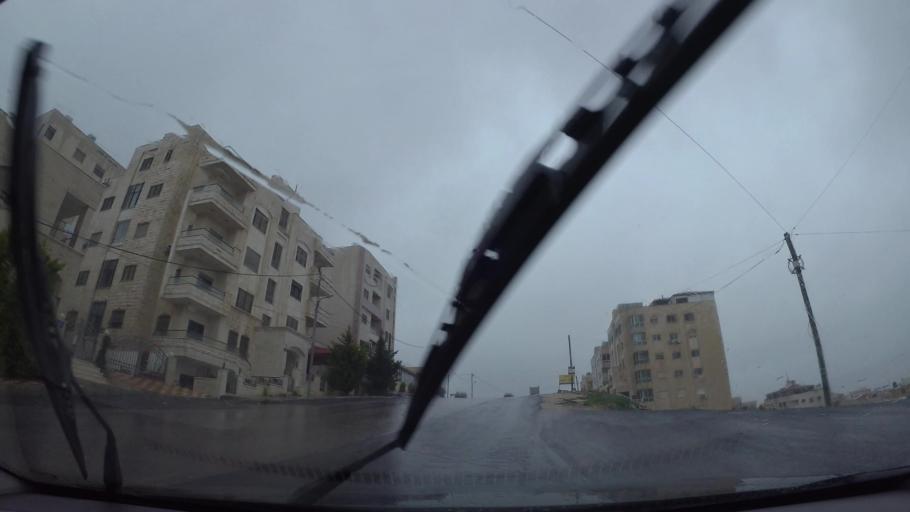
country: JO
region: Amman
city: Al Jubayhah
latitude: 32.0180
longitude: 35.8885
